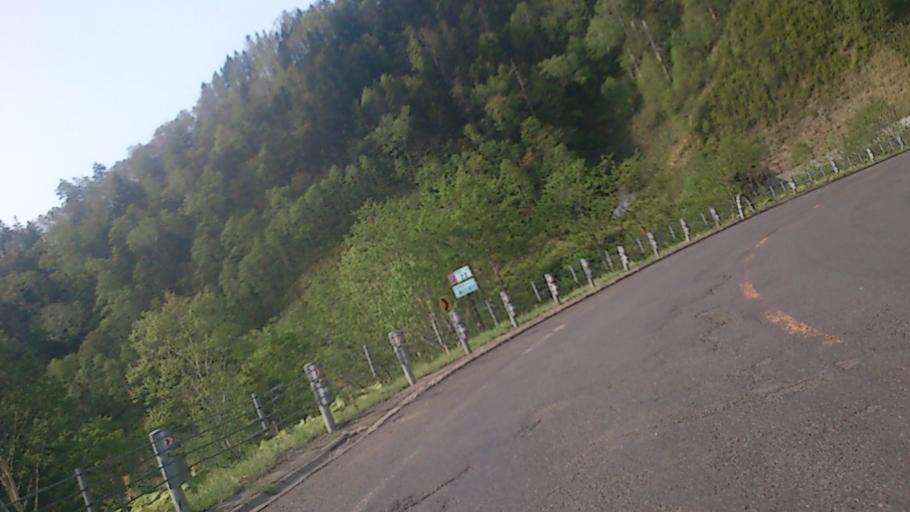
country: JP
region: Hokkaido
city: Bihoro
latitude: 43.4623
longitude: 144.2378
